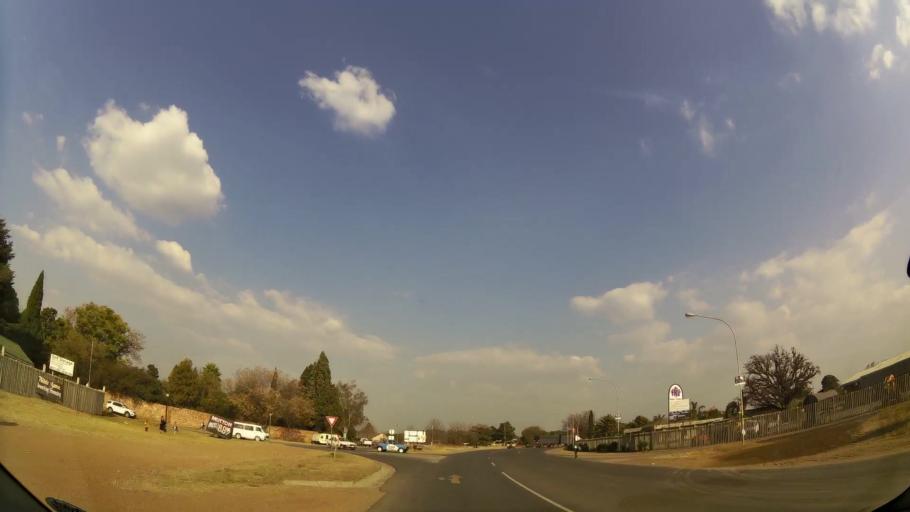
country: ZA
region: Gauteng
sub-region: Ekurhuleni Metropolitan Municipality
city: Benoni
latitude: -26.0950
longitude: 28.2972
